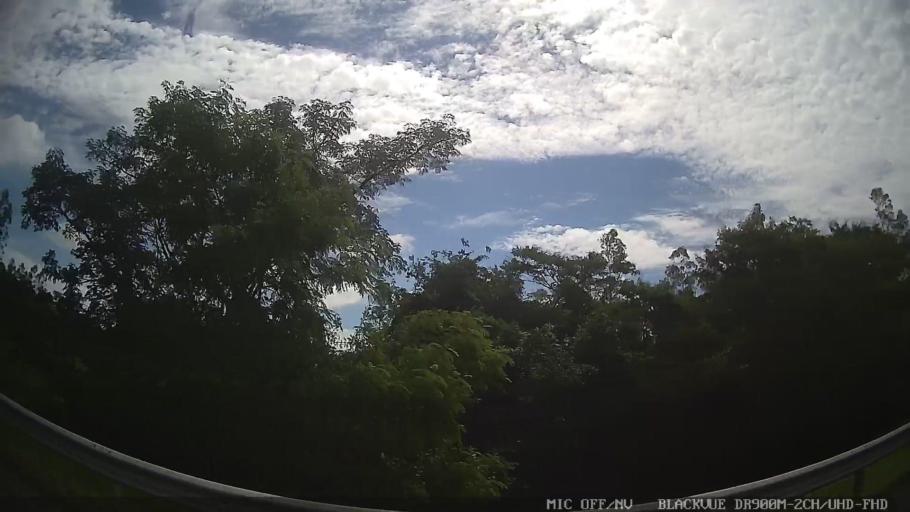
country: BR
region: Sao Paulo
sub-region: Laranjal Paulista
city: Laranjal Paulista
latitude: -23.0599
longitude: -47.8230
